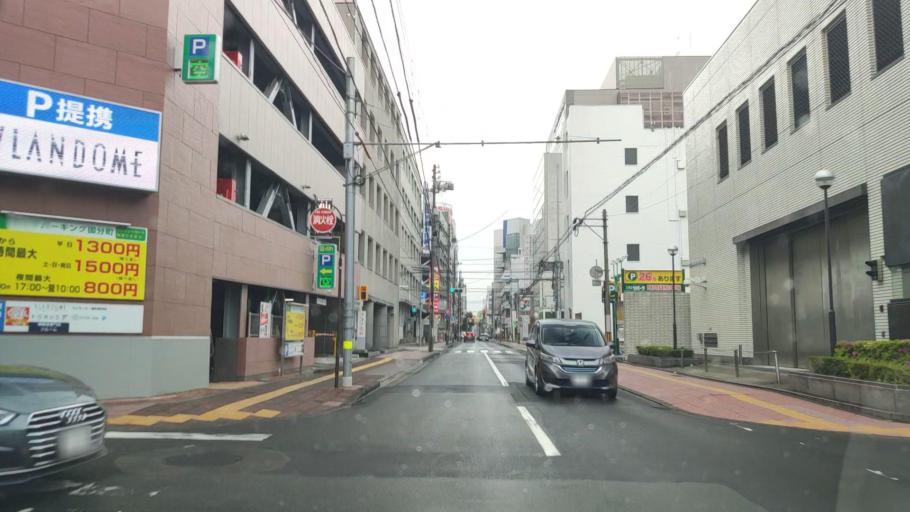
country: JP
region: Miyagi
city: Sendai
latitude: 38.2605
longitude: 140.8706
